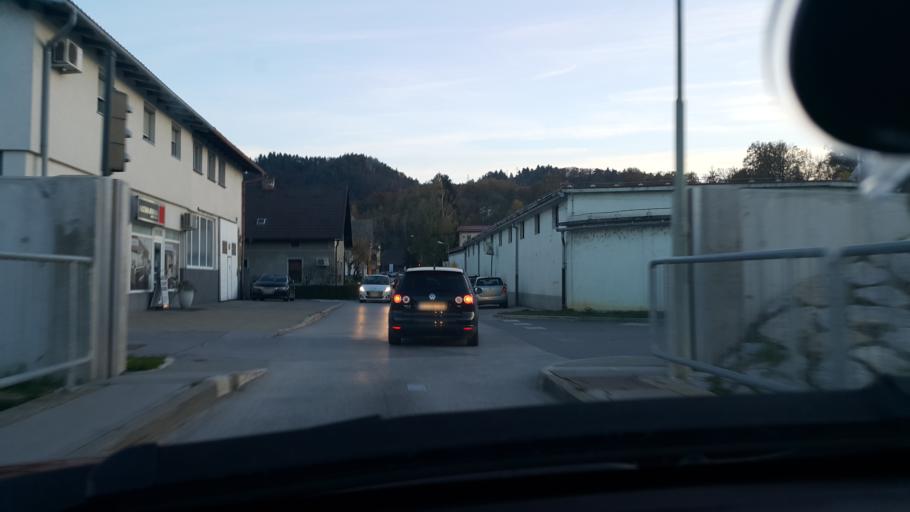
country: SI
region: Celje
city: Celje
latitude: 46.2323
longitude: 15.2781
